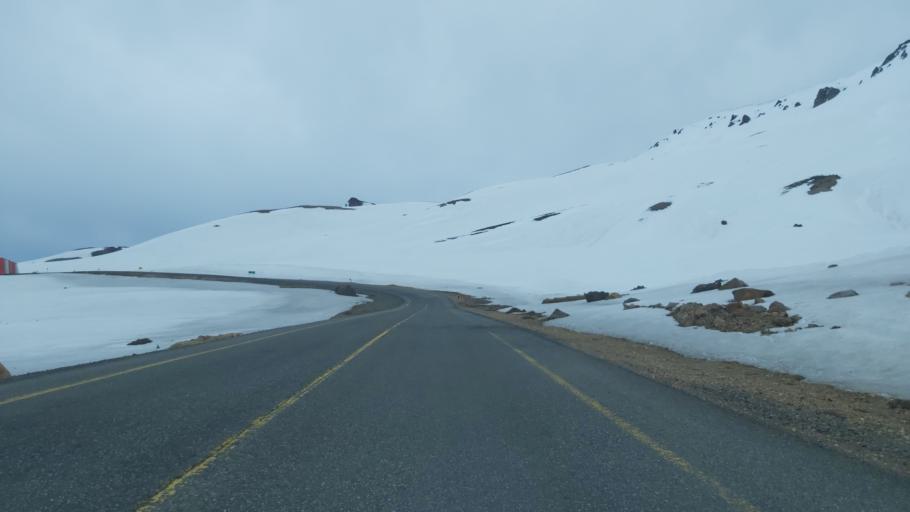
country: CL
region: Maule
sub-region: Provincia de Linares
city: Colbun
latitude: -36.0070
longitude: -70.4770
